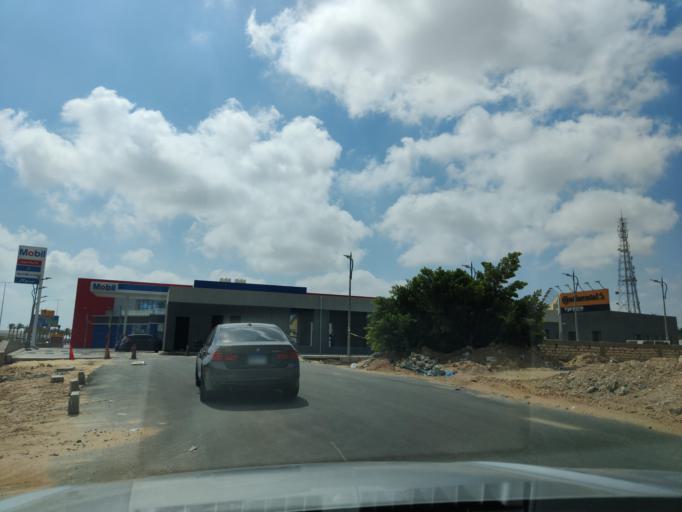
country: EG
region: Muhafazat Matruh
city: Al `Alamayn
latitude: 30.8450
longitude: 28.9400
